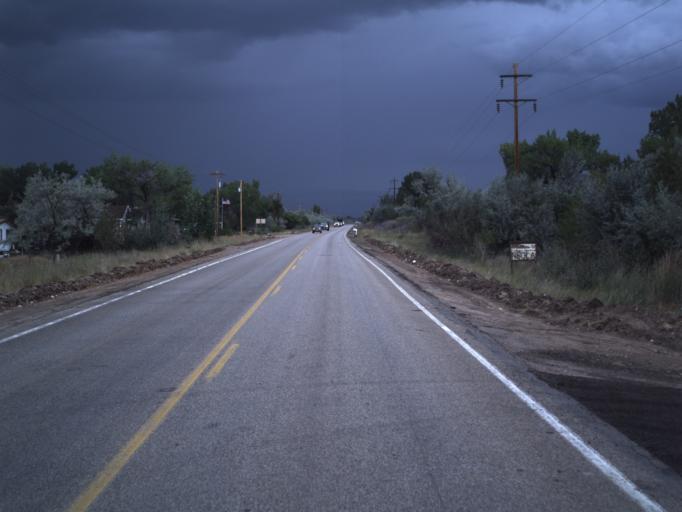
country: US
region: Utah
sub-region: Duchesne County
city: Roosevelt
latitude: 40.3713
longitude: -110.0297
